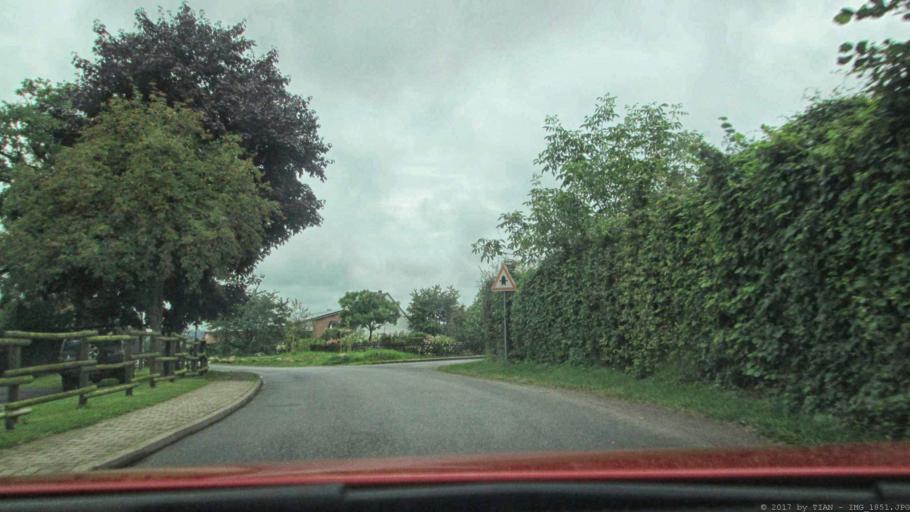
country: DE
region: Lower Saxony
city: Barum
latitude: 53.0479
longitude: 10.5410
